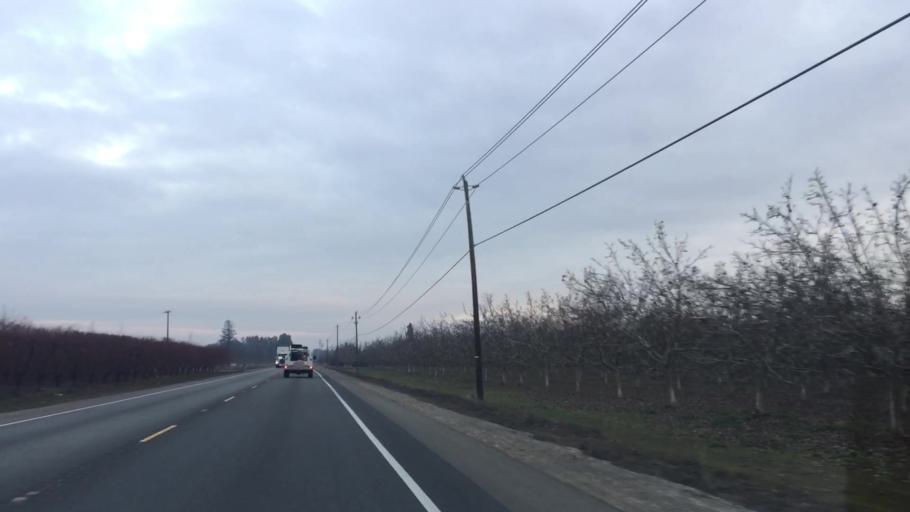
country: US
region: California
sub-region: Sutter County
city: Live Oak
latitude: 39.2965
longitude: -121.5950
